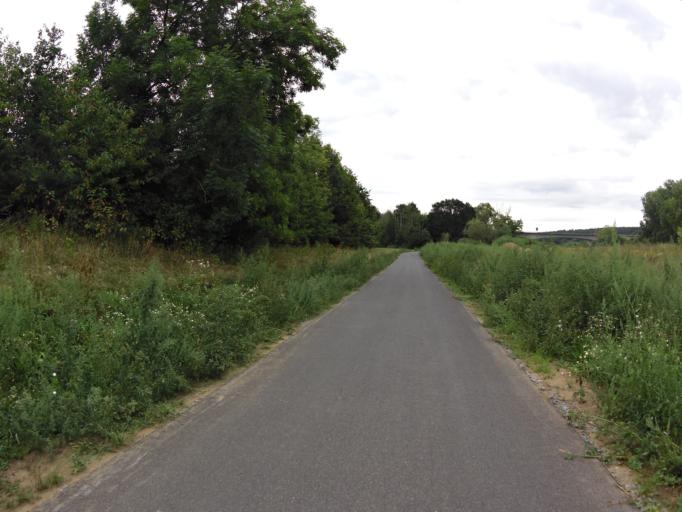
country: DE
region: Bavaria
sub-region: Regierungsbezirk Unterfranken
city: Schonungen
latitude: 50.0289
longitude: 10.3236
